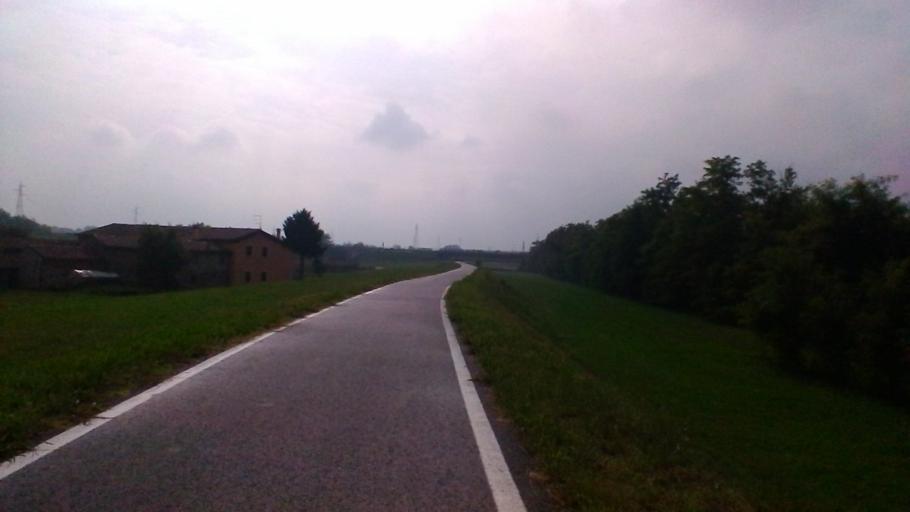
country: IT
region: Veneto
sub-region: Provincia di Verona
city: San Giovanni Lupatoto
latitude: 45.4055
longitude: 11.0318
